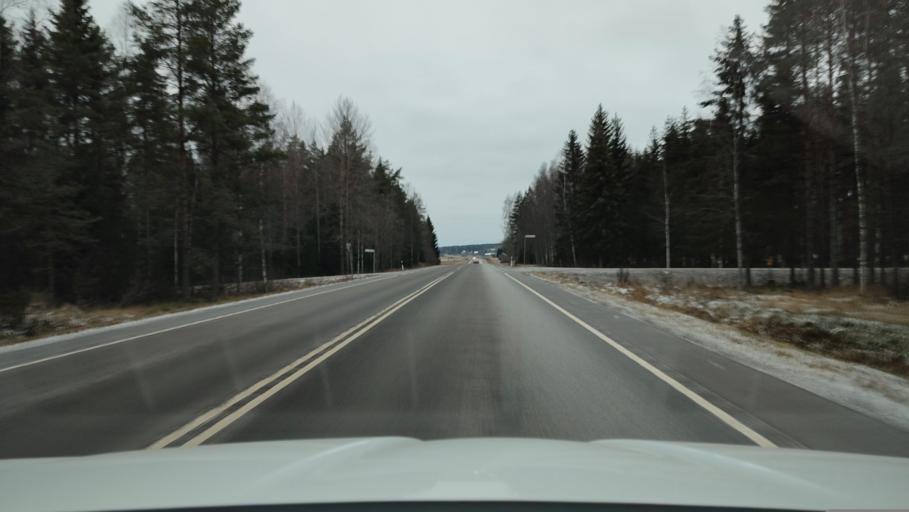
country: FI
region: Ostrobothnia
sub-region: Vaasa
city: Ristinummi
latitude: 62.9391
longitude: 21.7552
